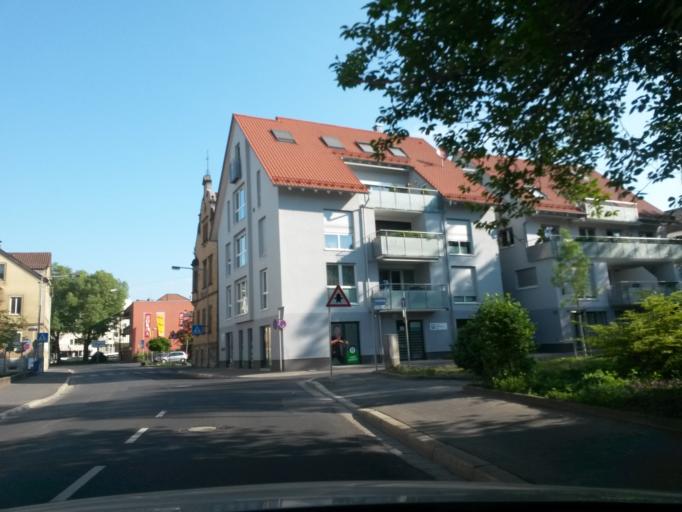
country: DE
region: Bavaria
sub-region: Regierungsbezirk Unterfranken
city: Bad Kissingen
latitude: 50.2009
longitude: 10.0811
